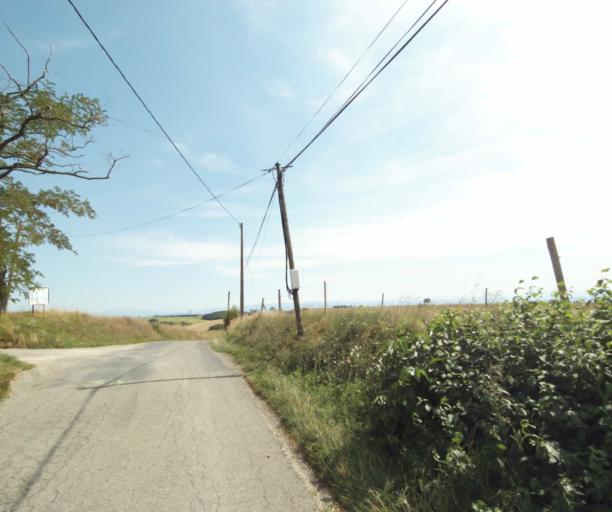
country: FR
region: Midi-Pyrenees
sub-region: Departement de la Haute-Garonne
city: Gaillac-Toulza
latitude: 43.2571
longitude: 1.4211
